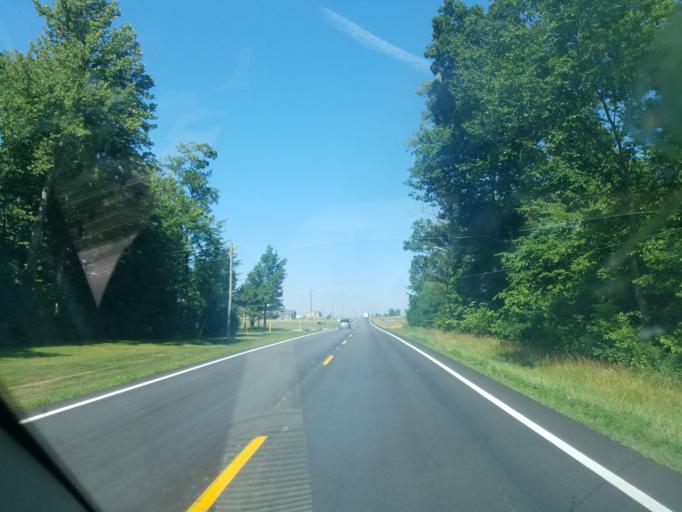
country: US
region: Ohio
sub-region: Shelby County
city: Jackson Center
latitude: 40.4394
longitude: -84.1013
